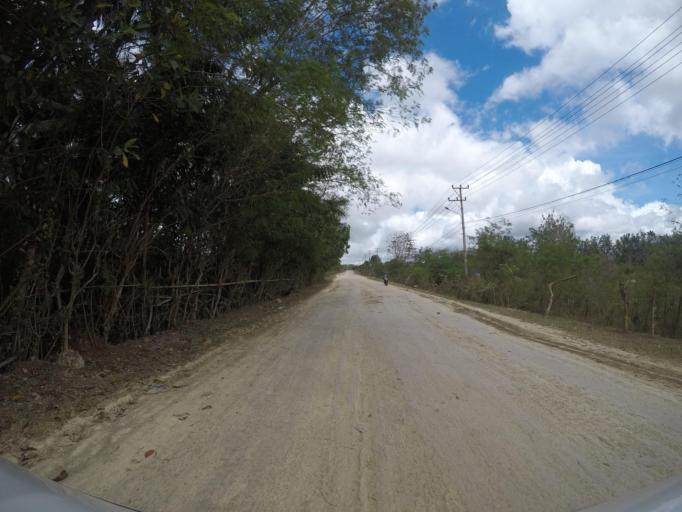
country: TL
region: Lautem
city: Lospalos
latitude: -8.4754
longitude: 126.9928
